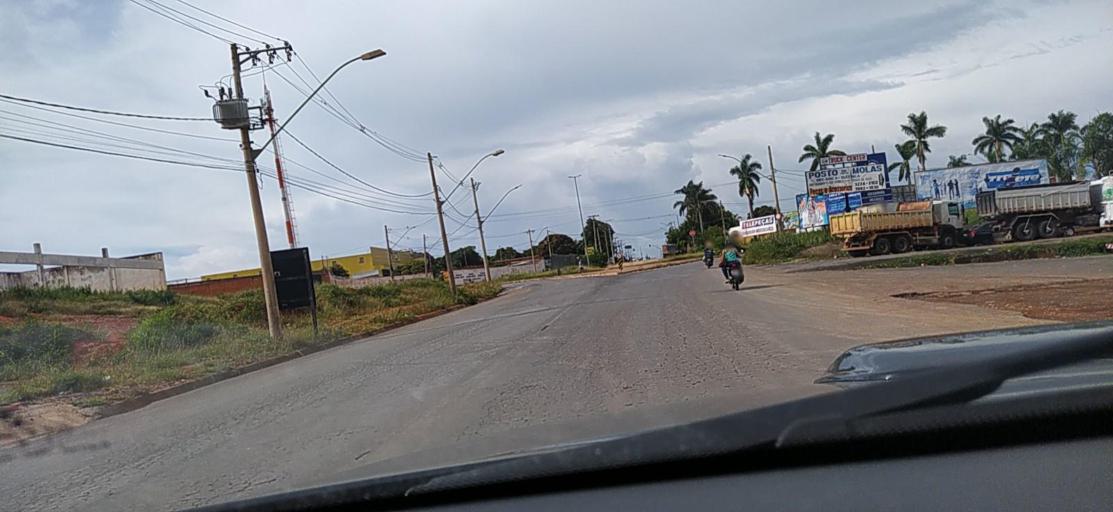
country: BR
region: Minas Gerais
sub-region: Montes Claros
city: Montes Claros
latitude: -16.7469
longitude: -43.8464
